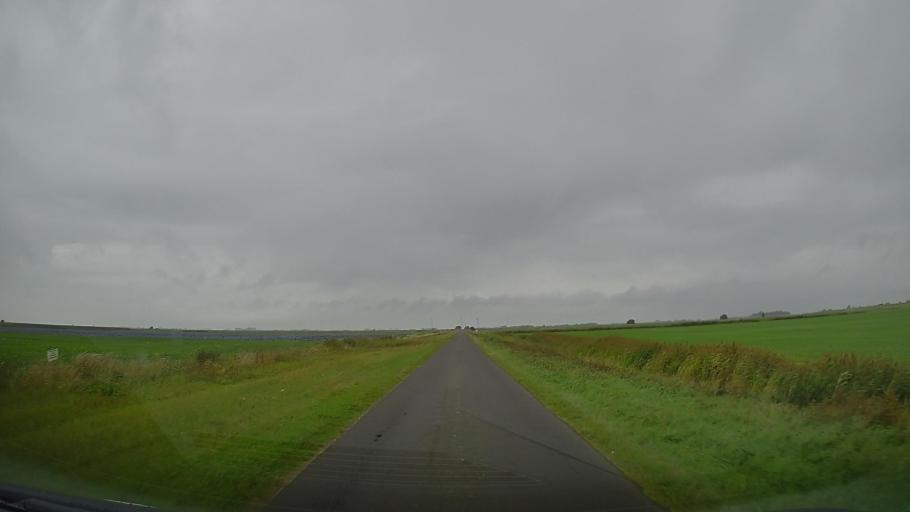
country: DE
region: Schleswig-Holstein
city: Friedrichsgabekoog
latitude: 54.1140
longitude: 8.9802
